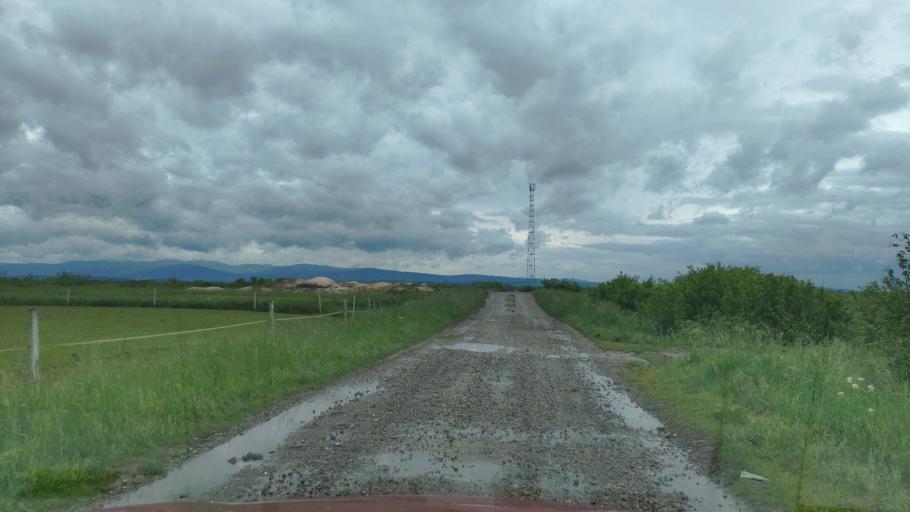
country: SK
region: Kosicky
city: Moldava nad Bodvou
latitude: 48.5437
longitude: 21.1126
